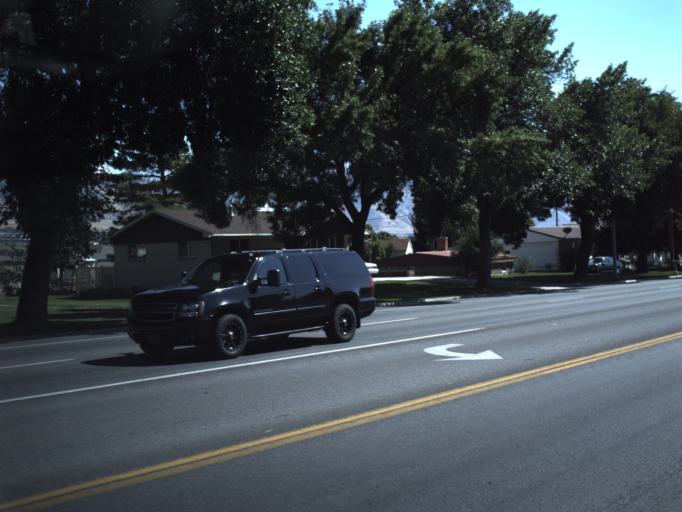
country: US
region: Utah
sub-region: Cache County
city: Smithfield
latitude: 41.8237
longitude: -111.8331
